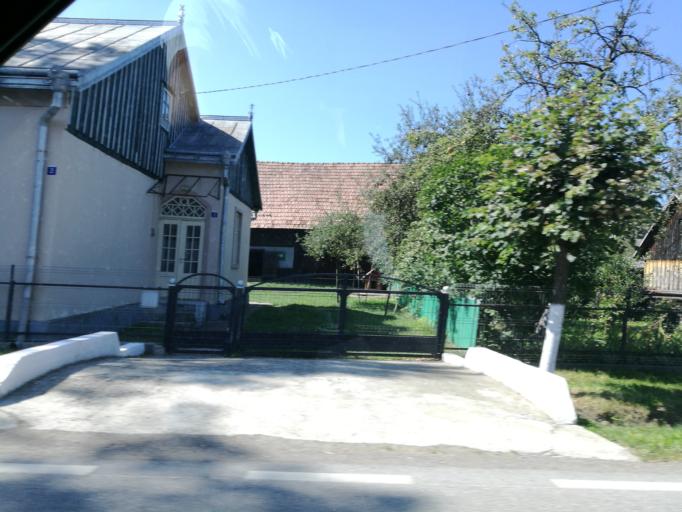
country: RO
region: Suceava
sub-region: Comuna Putna
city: Putna
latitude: 47.8754
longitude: 25.6141
